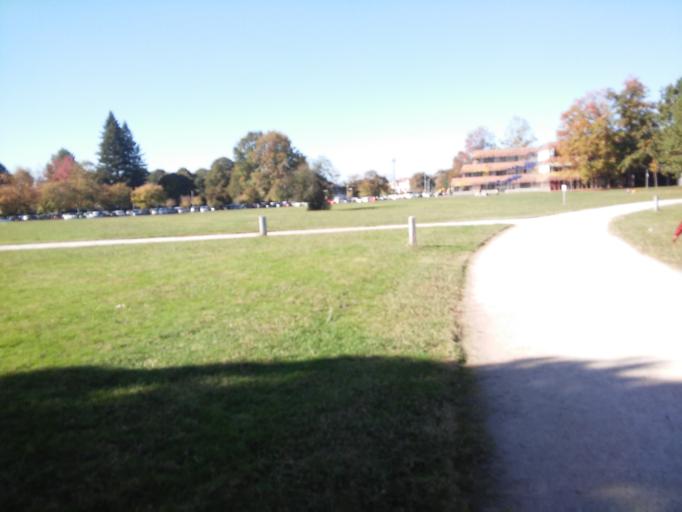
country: FR
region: Aquitaine
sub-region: Departement des Pyrenees-Atlantiques
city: Pau
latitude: 43.3145
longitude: -0.3660
